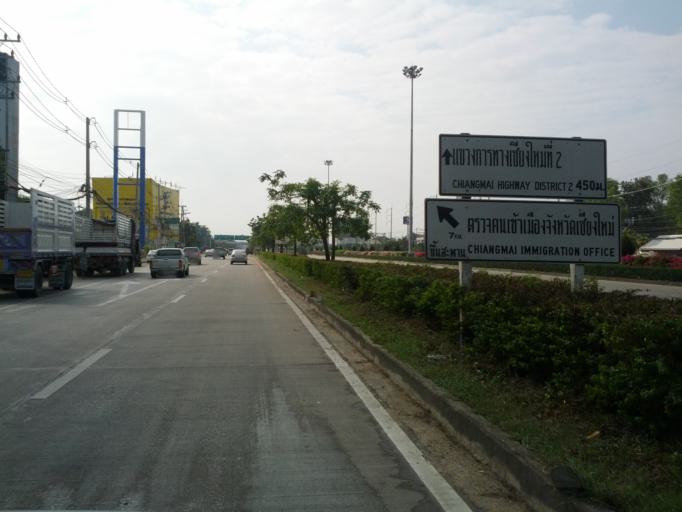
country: TH
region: Chiang Mai
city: Chiang Mai
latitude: 18.7704
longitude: 99.0288
